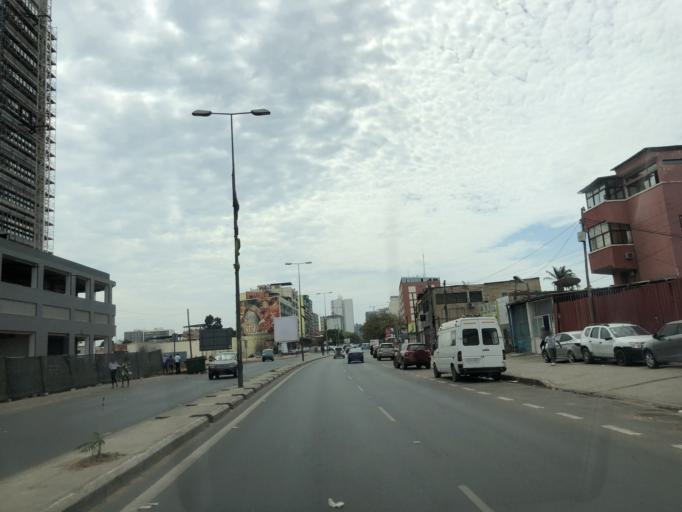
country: AO
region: Luanda
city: Luanda
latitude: -8.8245
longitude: 13.2551
